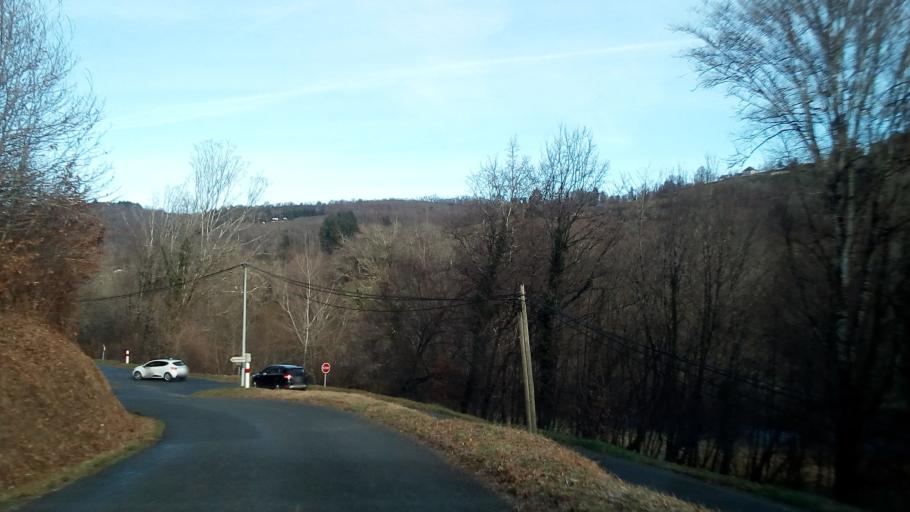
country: FR
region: Limousin
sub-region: Departement de la Correze
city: Naves
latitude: 45.3002
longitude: 1.7978
